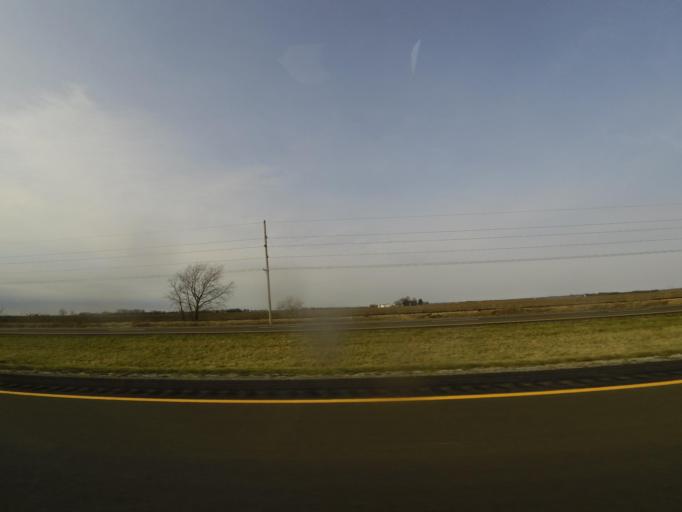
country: US
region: Illinois
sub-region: Christian County
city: Assumption
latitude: 39.5706
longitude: -89.0354
